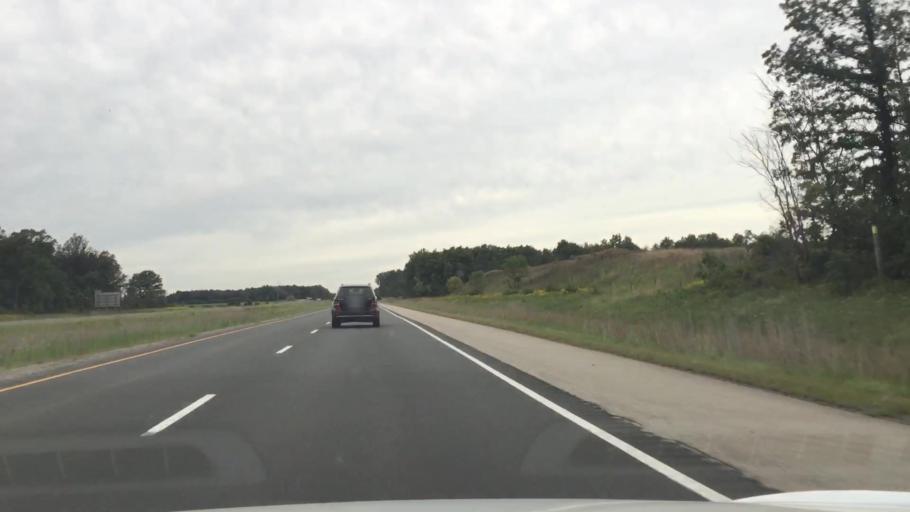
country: CA
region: Ontario
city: Lambton Shores
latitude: 42.9922
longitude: -81.8943
